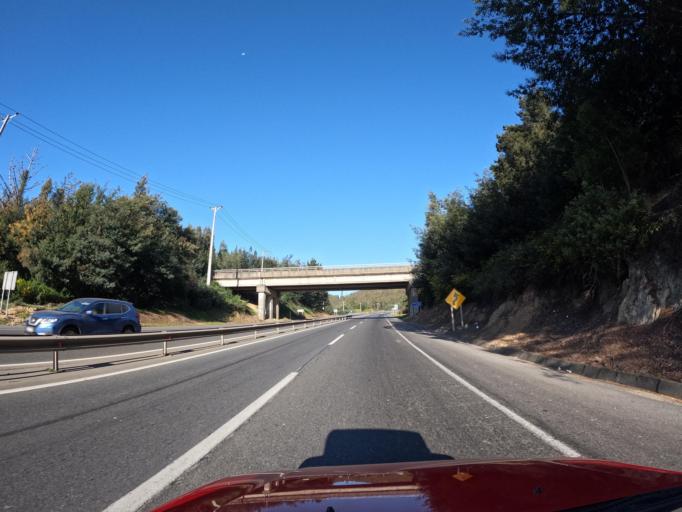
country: CL
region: Biobio
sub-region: Provincia de Concepcion
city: Penco
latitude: -36.7534
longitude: -72.9812
